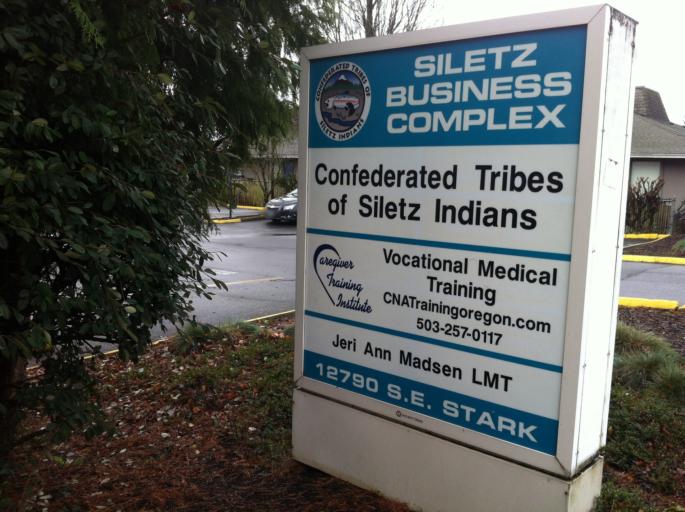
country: US
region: Oregon
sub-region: Multnomah County
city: Lents
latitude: 45.5190
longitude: -122.5324
